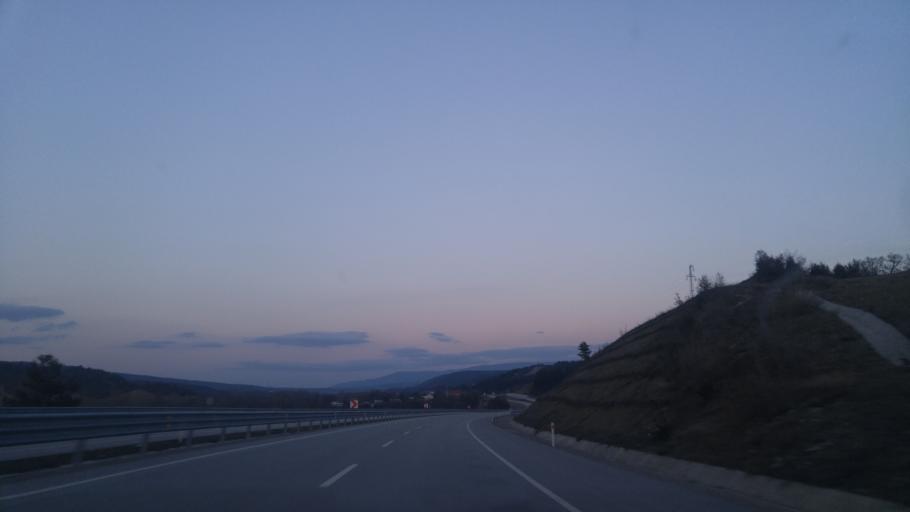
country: TR
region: Kastamonu
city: Igdir
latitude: 41.2322
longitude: 33.0738
